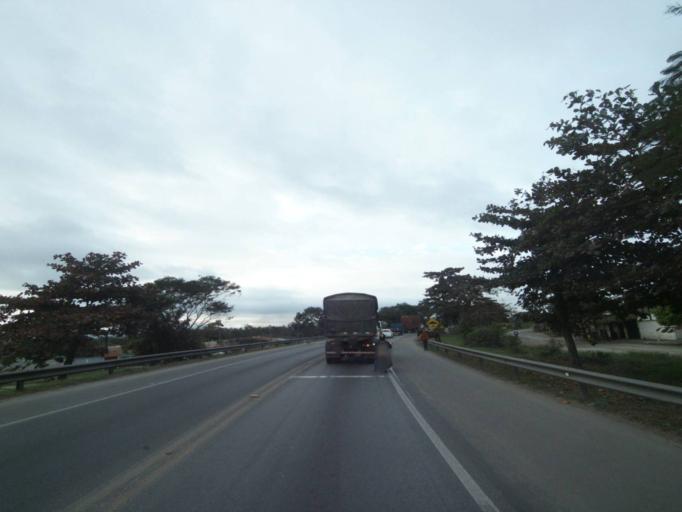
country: BR
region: Parana
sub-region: Paranagua
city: Paranagua
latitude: -25.5231
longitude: -48.5473
